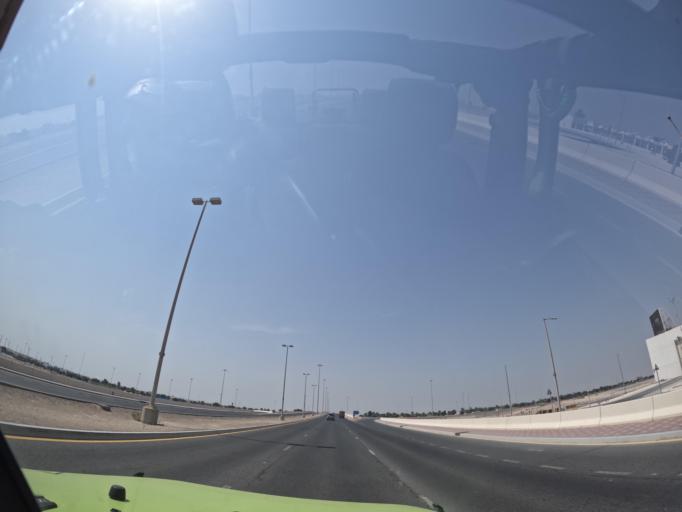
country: AE
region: Abu Dhabi
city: Abu Dhabi
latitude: 24.3380
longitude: 54.6402
